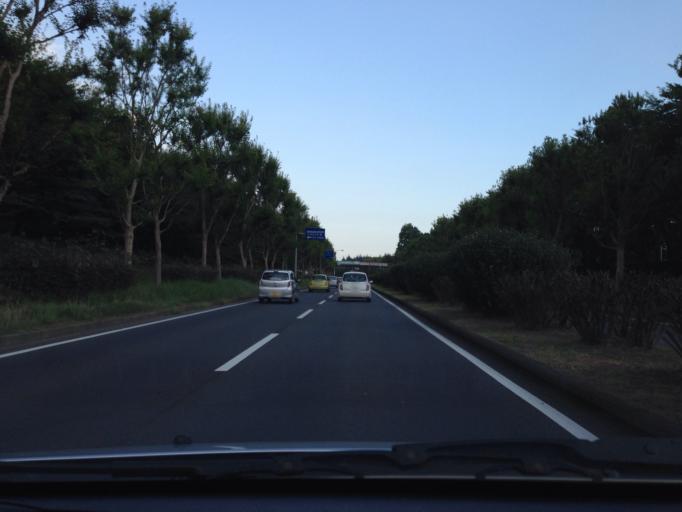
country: JP
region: Ibaraki
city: Naka
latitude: 36.0688
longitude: 140.1307
